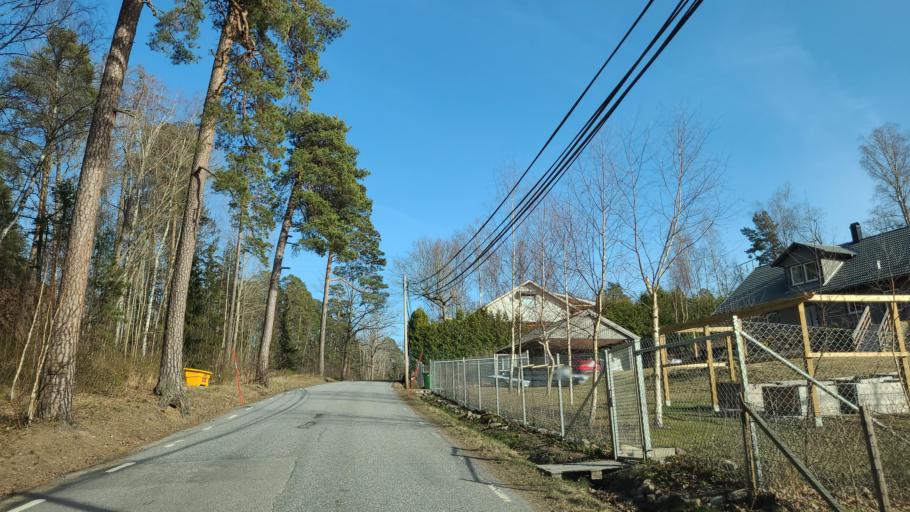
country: SE
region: Stockholm
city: Stenhamra
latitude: 59.2777
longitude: 17.6812
